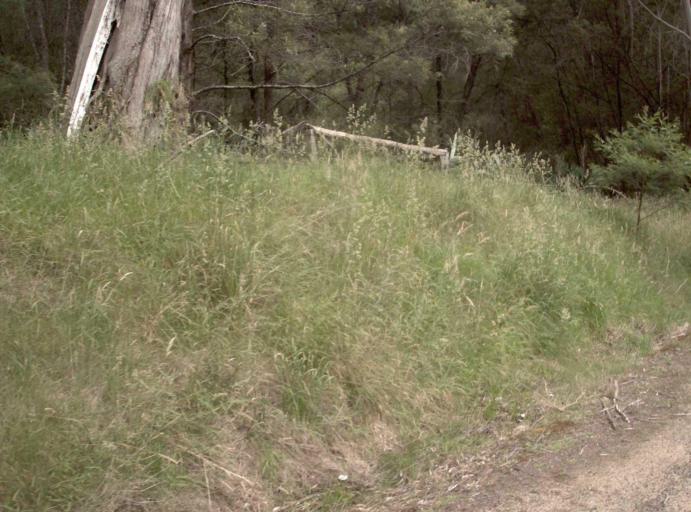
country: AU
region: New South Wales
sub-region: Bombala
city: Bombala
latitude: -37.4274
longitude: 149.1993
